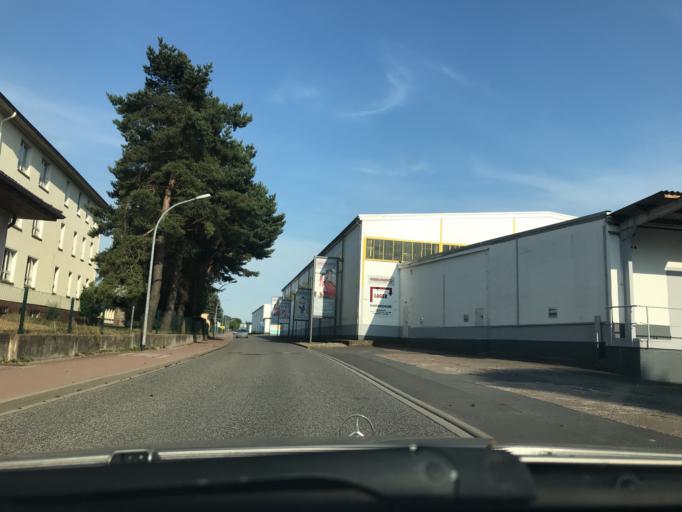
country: DE
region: Thuringia
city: Leinefelde
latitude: 51.3874
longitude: 10.3306
